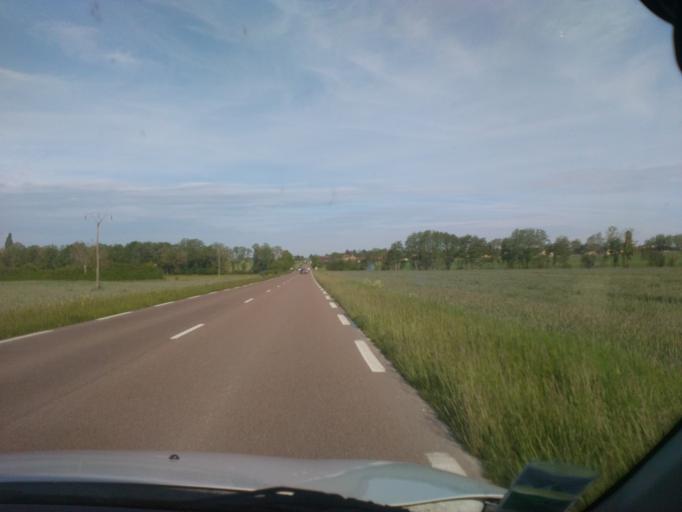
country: FR
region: Champagne-Ardenne
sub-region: Departement de l'Aube
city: Vendeuvre-sur-Barse
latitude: 48.2335
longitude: 4.4044
